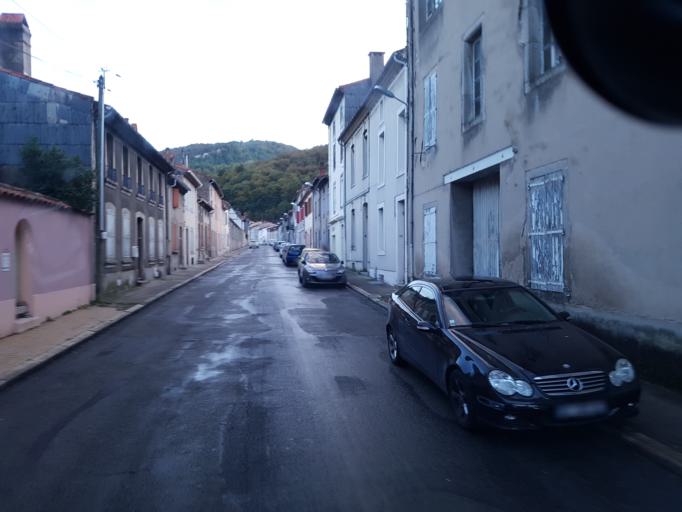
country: FR
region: Midi-Pyrenees
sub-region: Departement du Tarn
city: Mazamet
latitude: 43.4858
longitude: 2.3731
